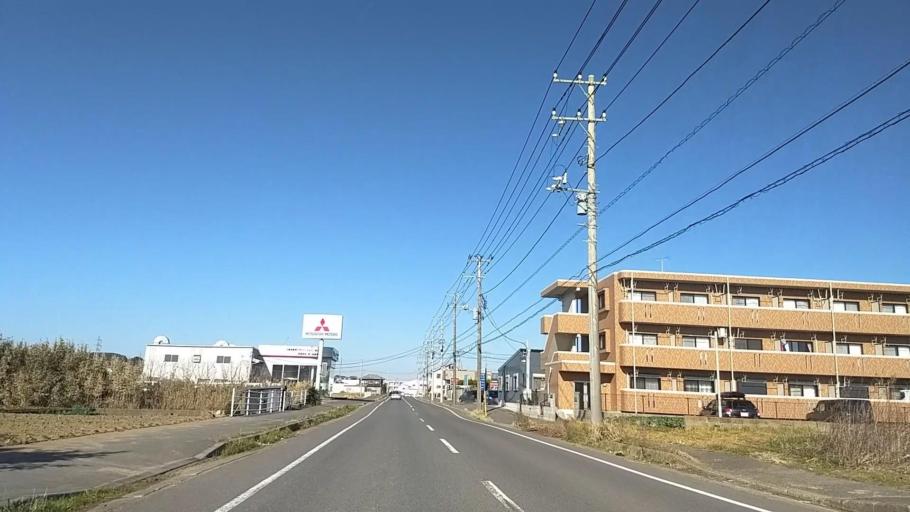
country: JP
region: Chiba
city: Hasaki
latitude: 35.7161
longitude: 140.8388
